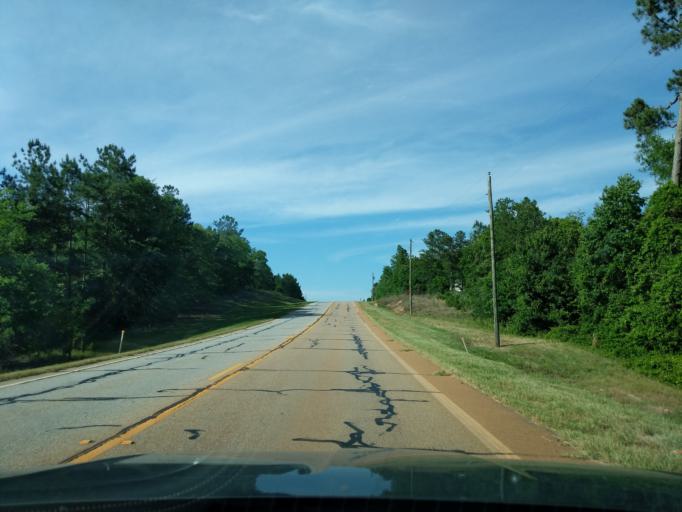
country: US
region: Georgia
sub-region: Jefferson County
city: Wrens
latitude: 33.2928
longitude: -82.3789
